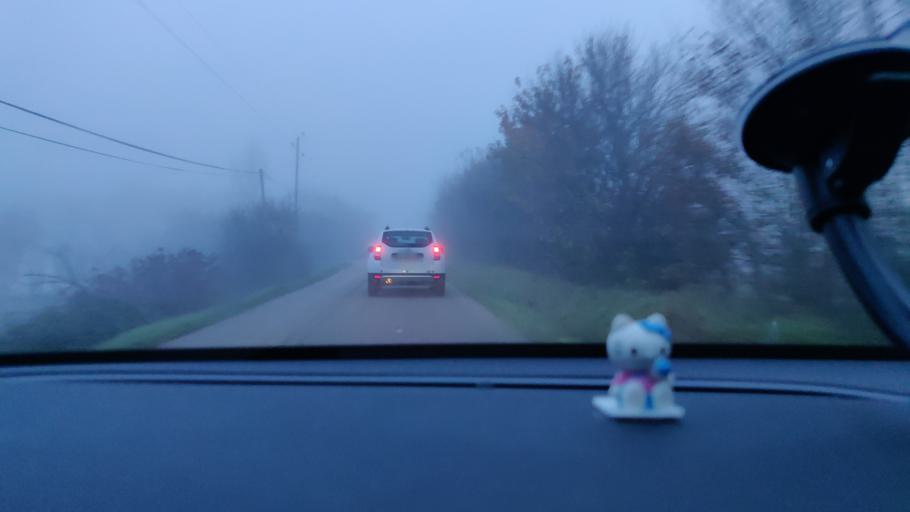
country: FR
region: Midi-Pyrenees
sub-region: Departement de la Haute-Garonne
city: Vieille-Toulouse
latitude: 43.4906
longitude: 1.4549
